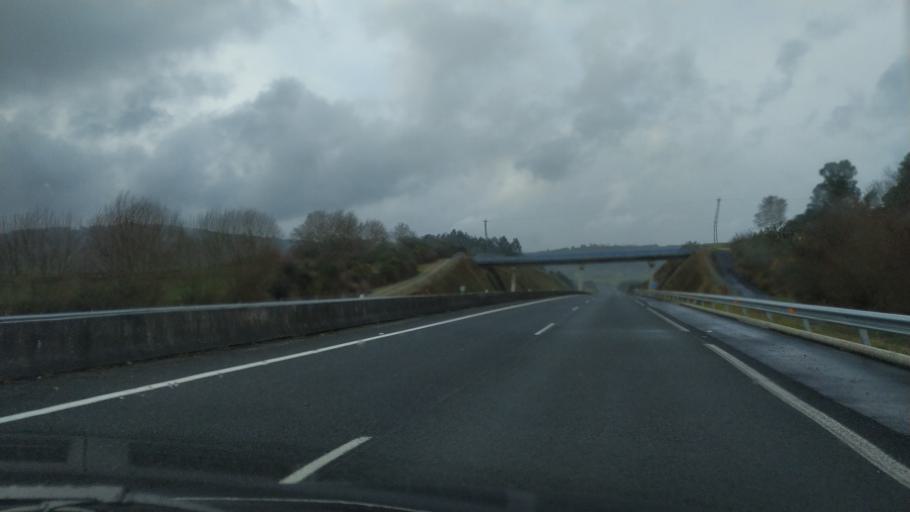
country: ES
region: Galicia
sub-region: Provincia de Pontevedra
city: Silleda
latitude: 42.7203
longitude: -8.3101
